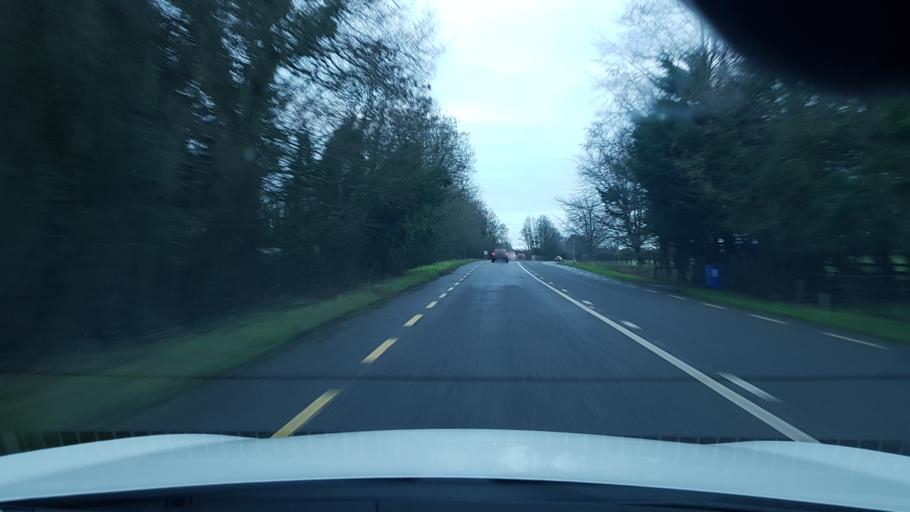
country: IE
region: Leinster
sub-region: An Mhi
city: Dunshaughlin
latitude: 53.5742
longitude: -6.5826
